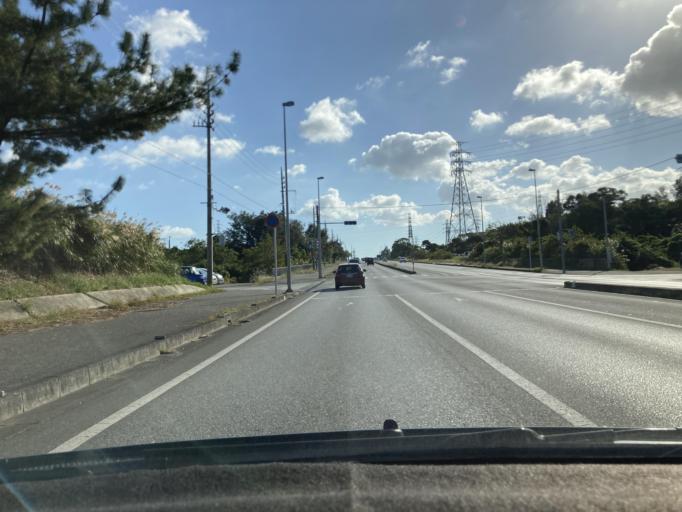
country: JP
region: Okinawa
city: Ishikawa
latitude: 26.3968
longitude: 127.8288
